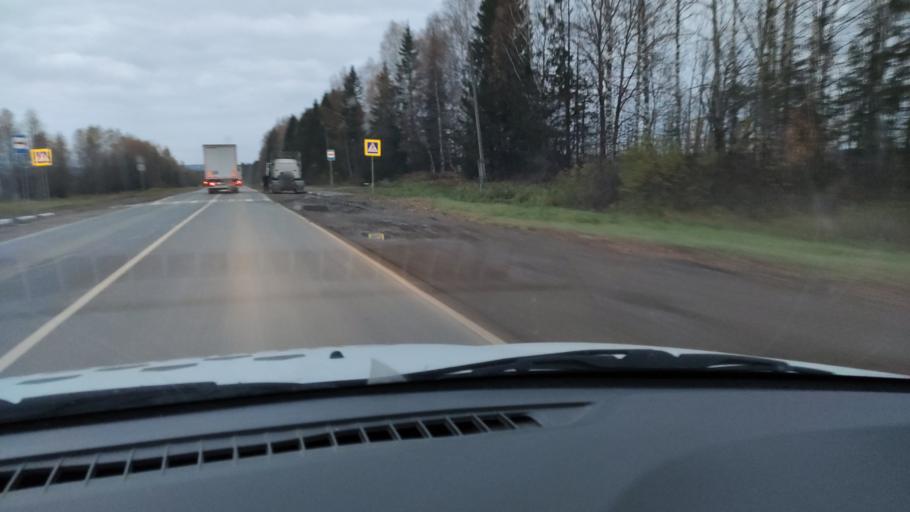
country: RU
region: Kirov
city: Kostino
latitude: 58.8576
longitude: 53.1854
